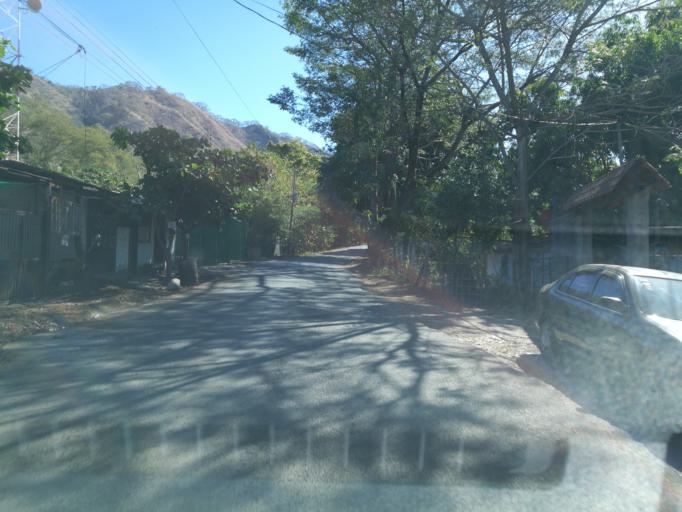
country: CR
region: Guanacaste
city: Juntas
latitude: 10.0987
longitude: -84.9888
